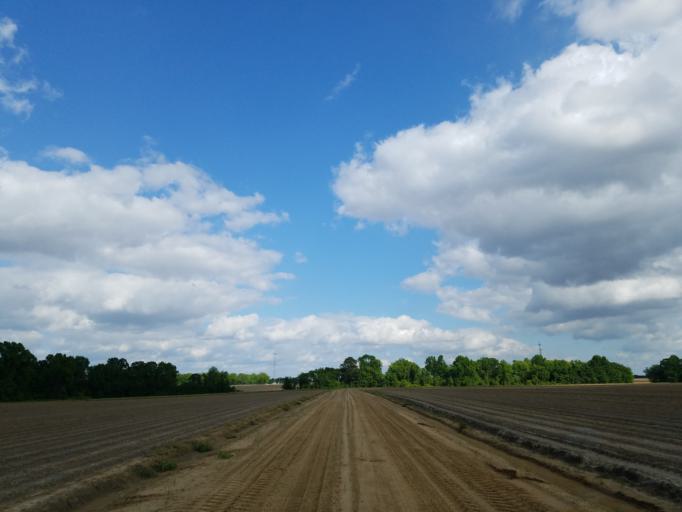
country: US
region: Georgia
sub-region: Dooly County
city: Vienna
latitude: 32.1754
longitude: -83.7775
